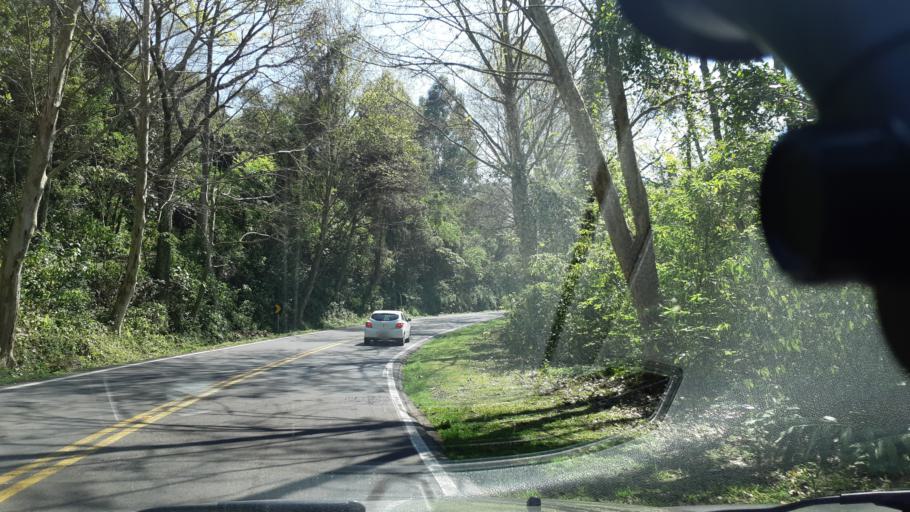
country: BR
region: Rio Grande do Sul
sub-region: Nova Petropolis
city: Nova Petropolis
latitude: -29.4014
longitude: -51.1267
